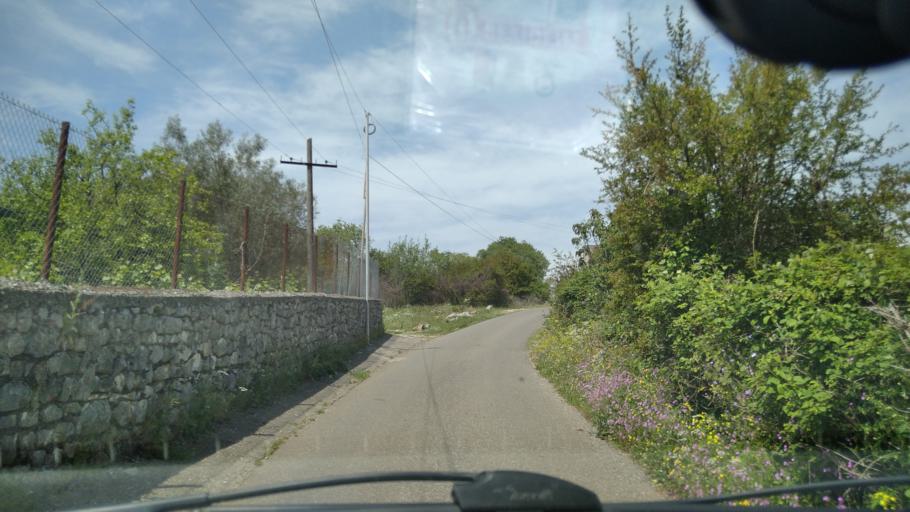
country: AL
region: Shkoder
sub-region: Rrethi i Malesia e Madhe
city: Gruemire
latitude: 42.1432
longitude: 19.5470
